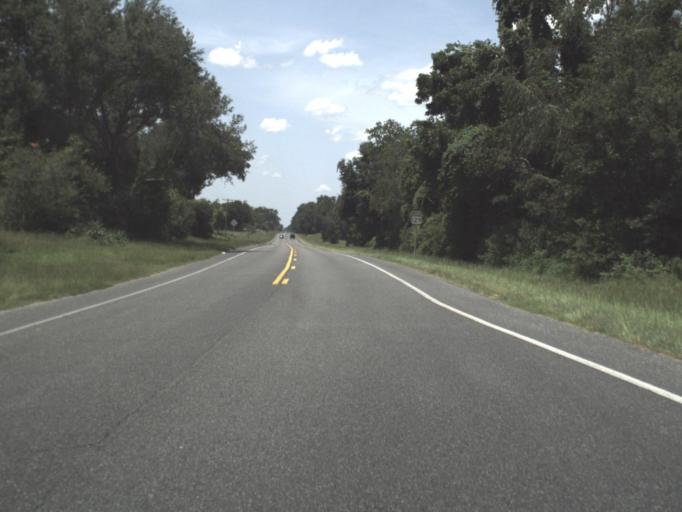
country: US
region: Florida
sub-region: Levy County
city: Chiefland
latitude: 29.5112
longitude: -82.8228
